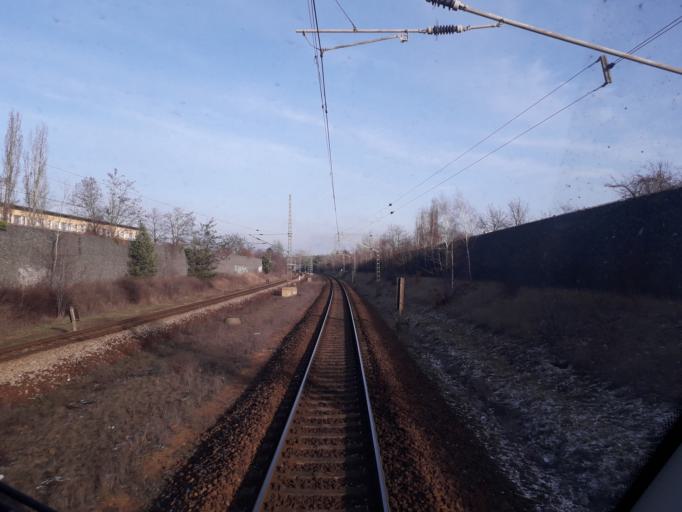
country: DE
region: Berlin
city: Altglienicke
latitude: 52.4050
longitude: 13.5418
